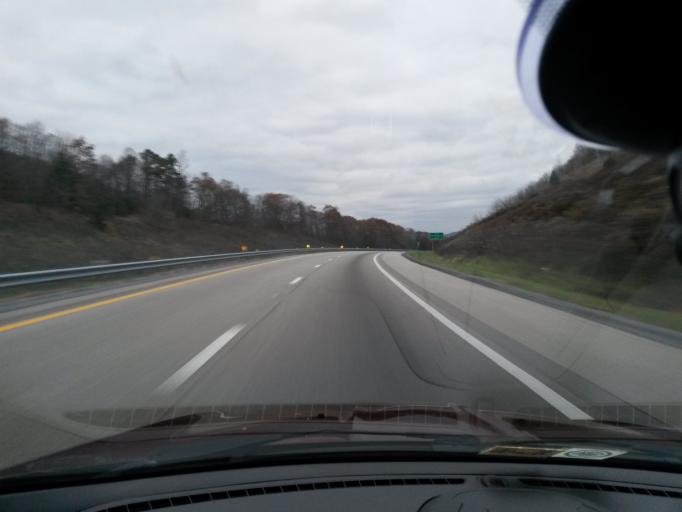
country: US
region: Virginia
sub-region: City of Lexington
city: Lexington
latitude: 37.8697
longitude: -79.6226
